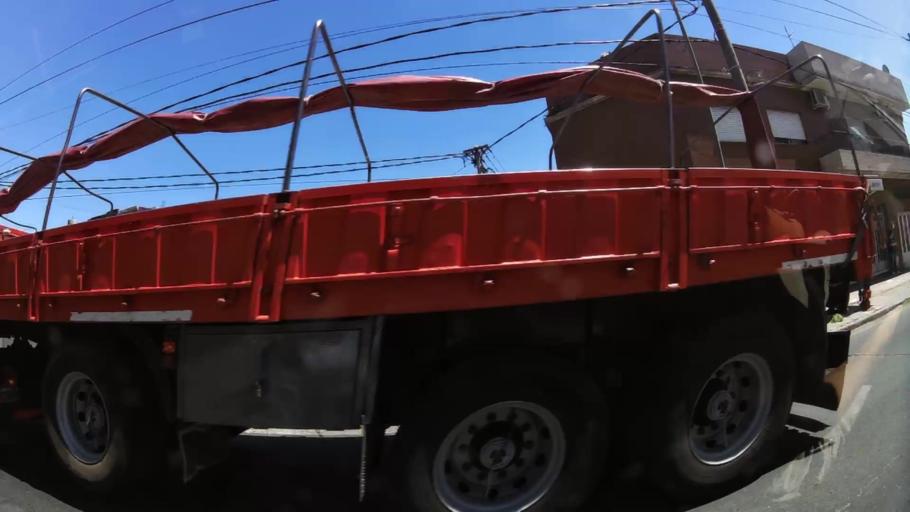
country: AR
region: Buenos Aires
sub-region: Partido de General San Martin
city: General San Martin
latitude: -34.5463
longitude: -58.5274
